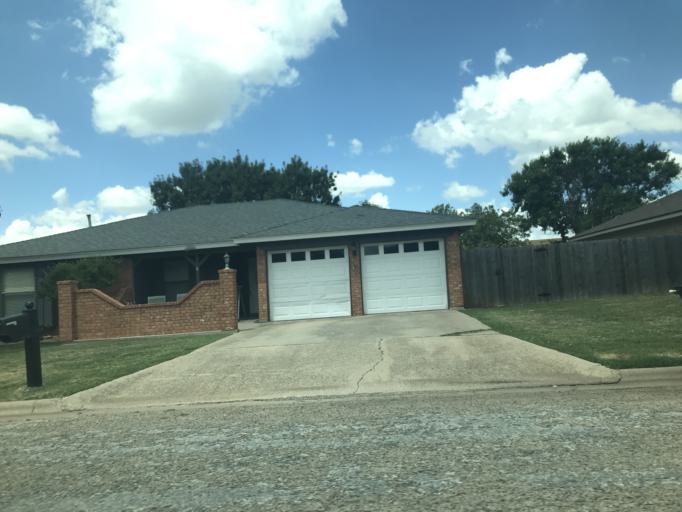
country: US
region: Texas
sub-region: Taylor County
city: Abilene
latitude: 32.4409
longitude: -99.7024
